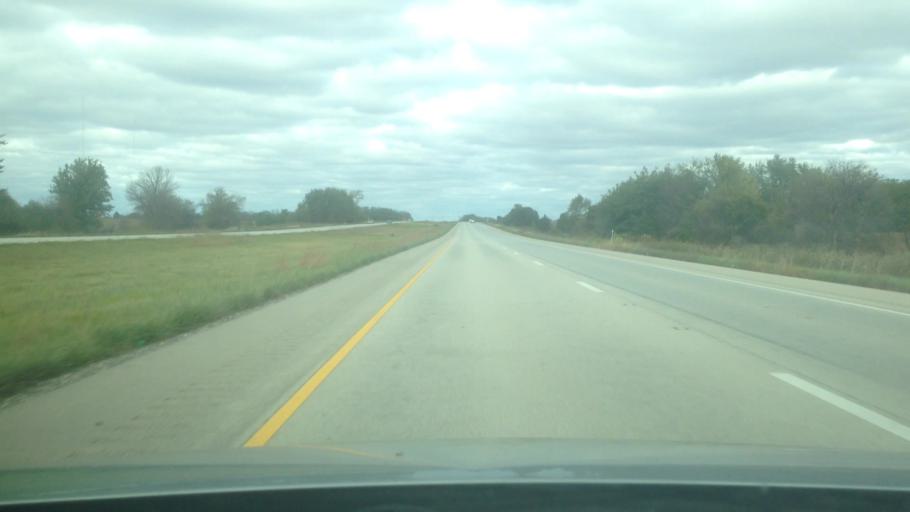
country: US
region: Illinois
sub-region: Macon County
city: Forsyth
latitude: 39.9227
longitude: -88.8546
